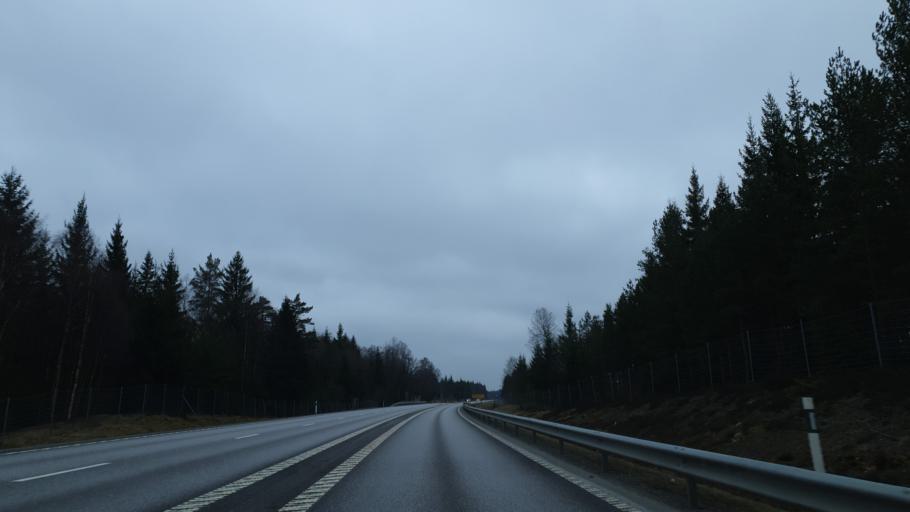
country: SE
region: Vaestra Goetaland
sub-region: Boras Kommun
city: Viskafors
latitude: 57.6338
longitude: 12.8983
